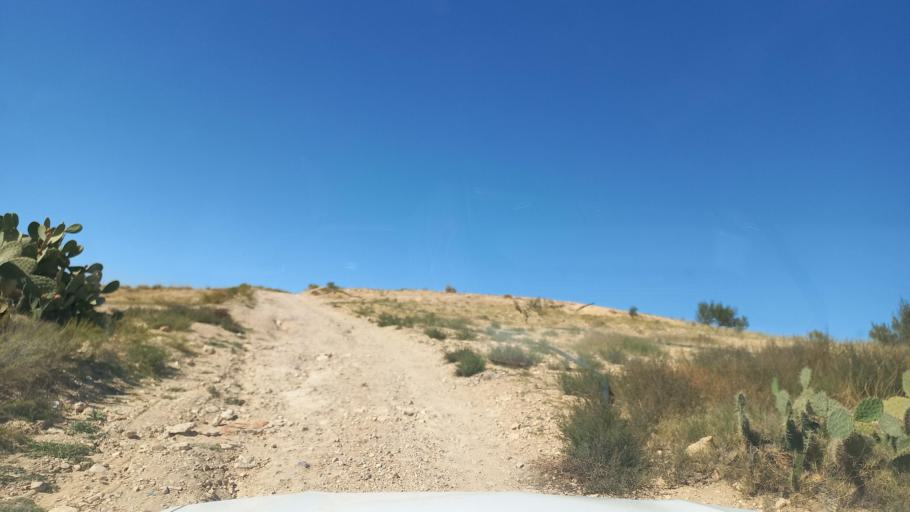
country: TN
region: Al Qasrayn
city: Sbiba
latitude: 35.3758
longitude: 9.0798
